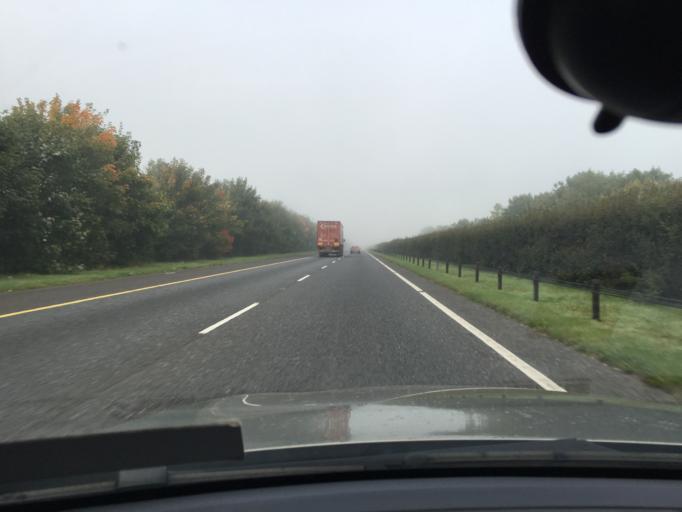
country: IE
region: Leinster
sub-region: Kildare
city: Maynooth
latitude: 53.3760
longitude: -6.6307
